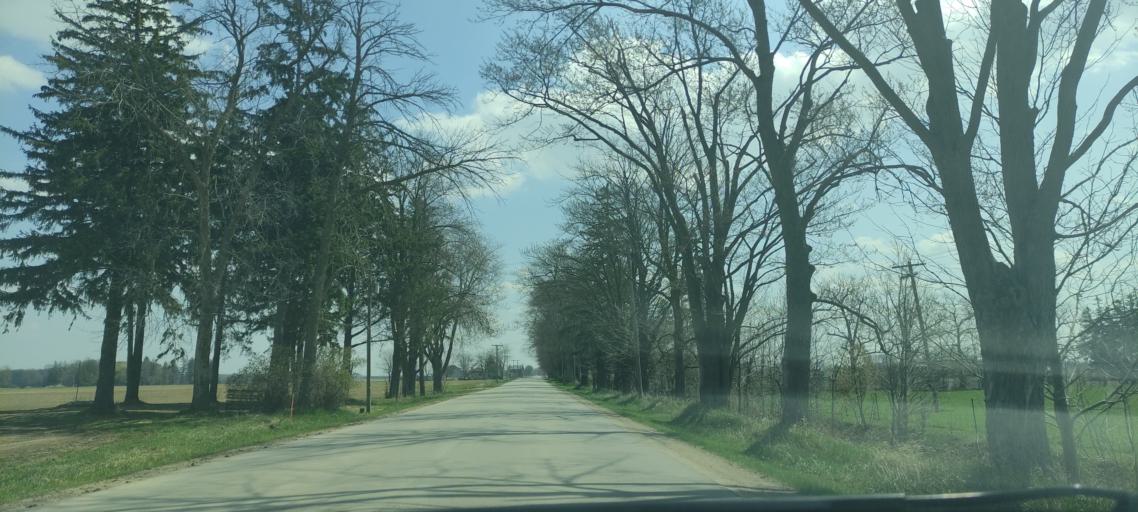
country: CA
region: Ontario
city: Stratford
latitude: 43.3347
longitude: -80.9728
